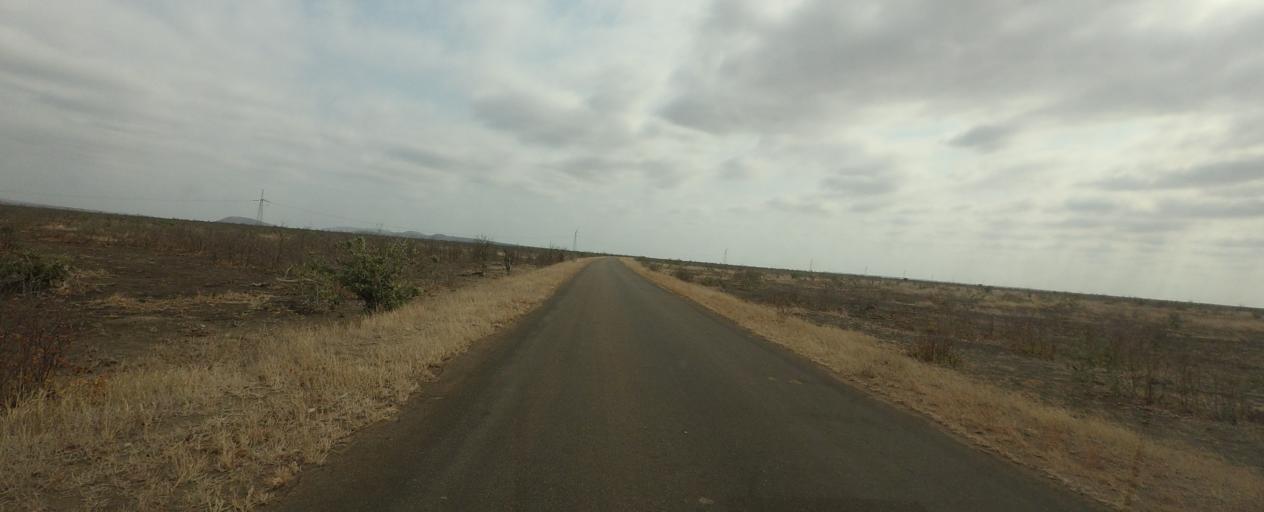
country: ZA
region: Limpopo
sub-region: Vhembe District Municipality
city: Mutale
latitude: -22.6661
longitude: 31.1678
